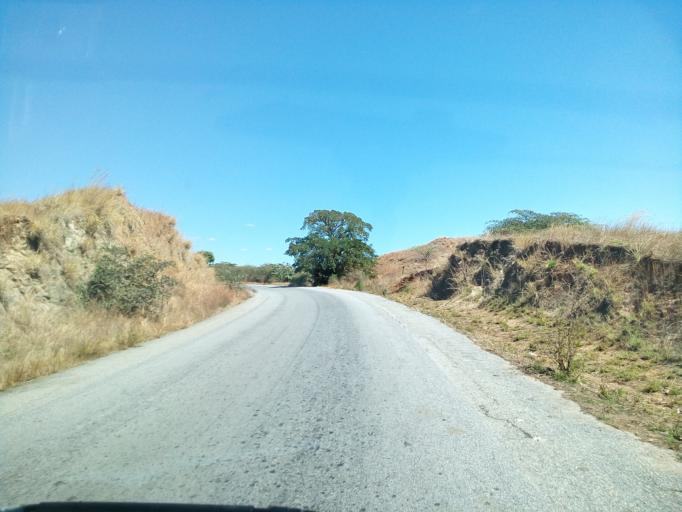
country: MG
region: Betsiboka
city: Maevatanana
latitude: -17.0708
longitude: 46.8022
